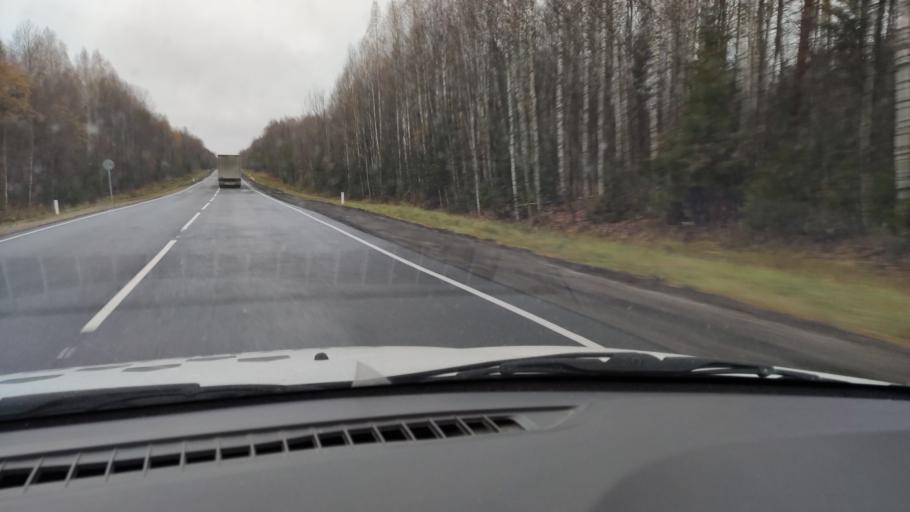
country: RU
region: Kirov
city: Omutninsk
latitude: 58.7648
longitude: 51.9879
